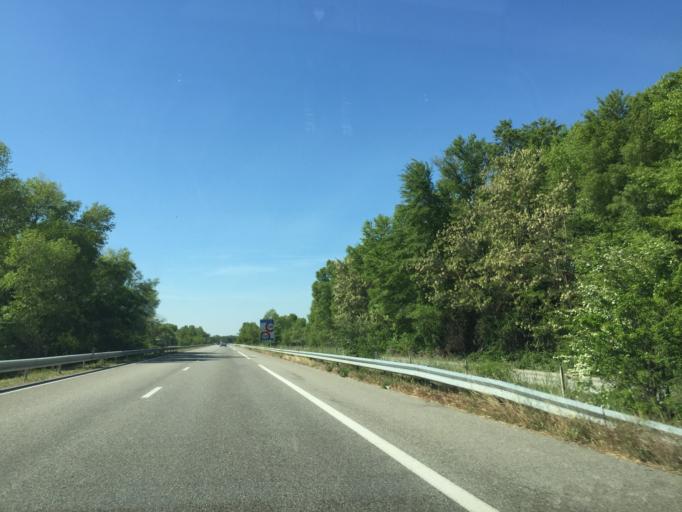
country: FR
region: Provence-Alpes-Cote d'Azur
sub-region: Departement des Alpes-de-Haute-Provence
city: Villeneuve
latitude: 43.8762
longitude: 5.8752
